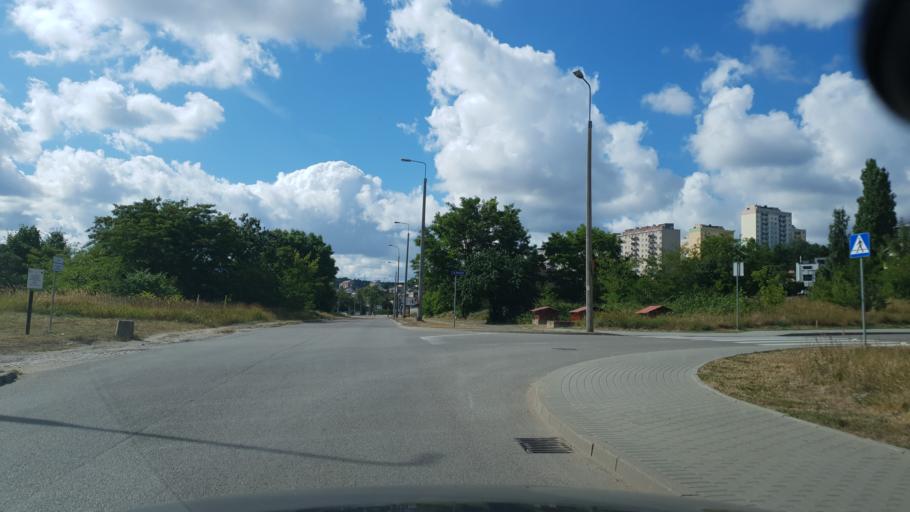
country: PL
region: Pomeranian Voivodeship
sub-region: Gdynia
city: Gdynia
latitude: 54.5467
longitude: 18.5200
